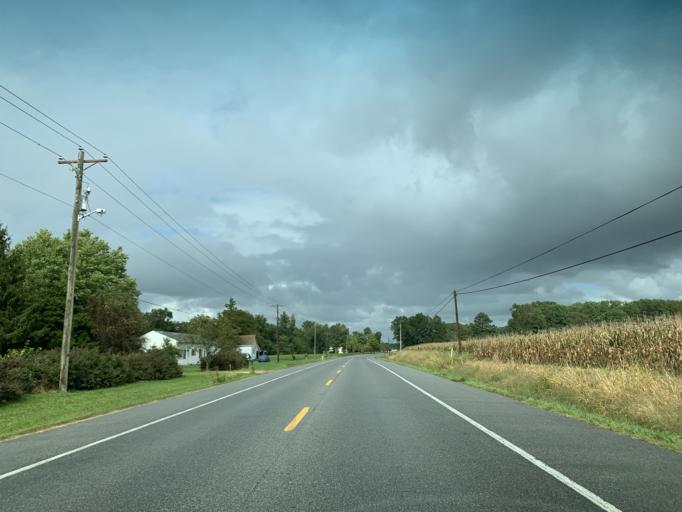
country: US
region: Maryland
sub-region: Caroline County
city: Ridgely
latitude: 38.9631
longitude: -75.8871
